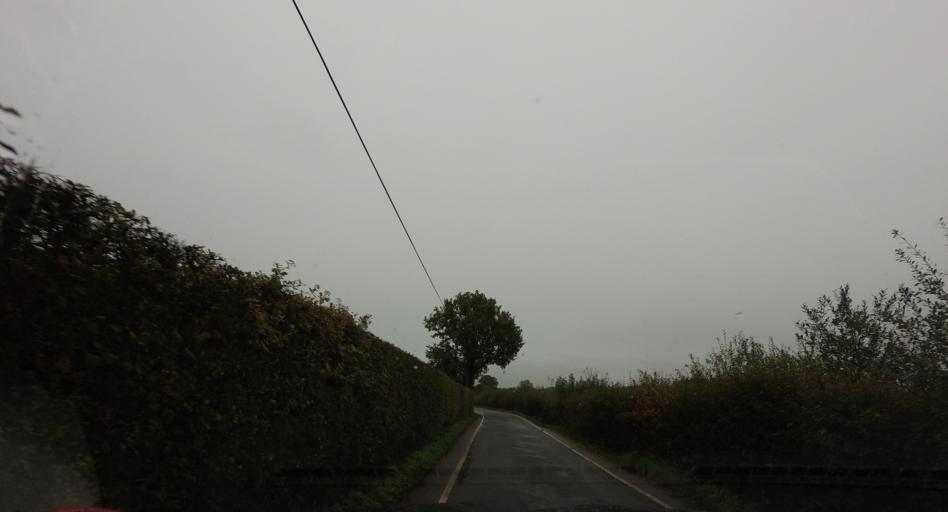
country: GB
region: England
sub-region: Kent
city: Tonbridge
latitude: 51.1886
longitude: 0.2485
